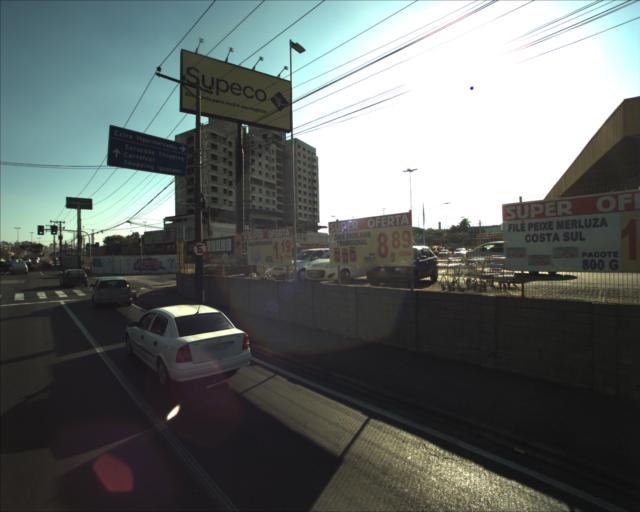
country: BR
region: Sao Paulo
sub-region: Sorocaba
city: Sorocaba
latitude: -23.4903
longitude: -47.4414
